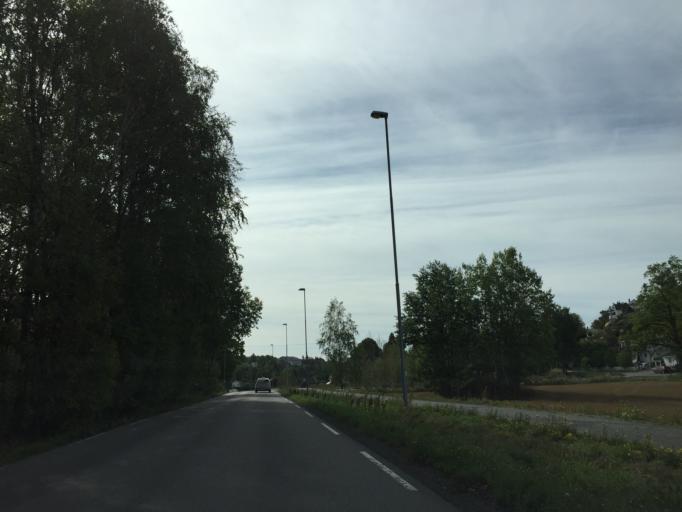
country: NO
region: Ostfold
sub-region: Moss
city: Moss
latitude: 59.4970
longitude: 10.6875
